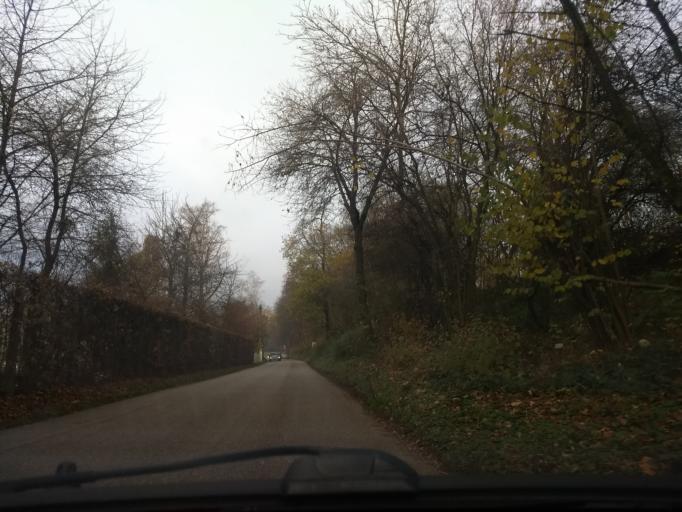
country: DE
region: Baden-Wuerttemberg
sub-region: Karlsruhe Region
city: Baden-Baden
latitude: 48.7906
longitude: 8.2140
